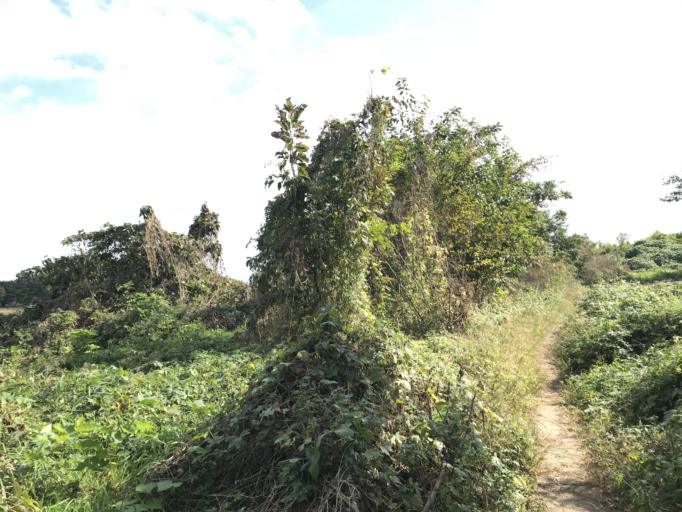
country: JP
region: Tokyo
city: Chofugaoka
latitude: 35.6322
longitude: 139.5627
